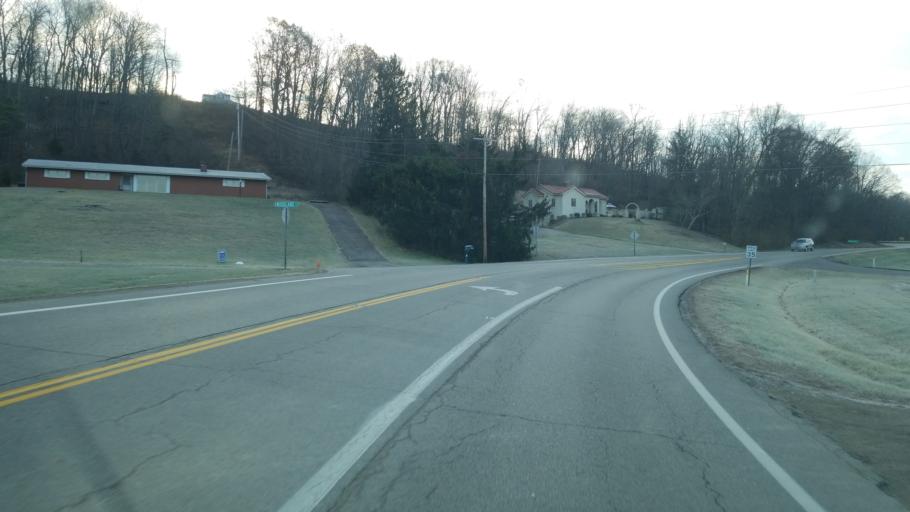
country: US
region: Ohio
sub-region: Ross County
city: North Fork Village
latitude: 39.3363
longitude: -83.0261
